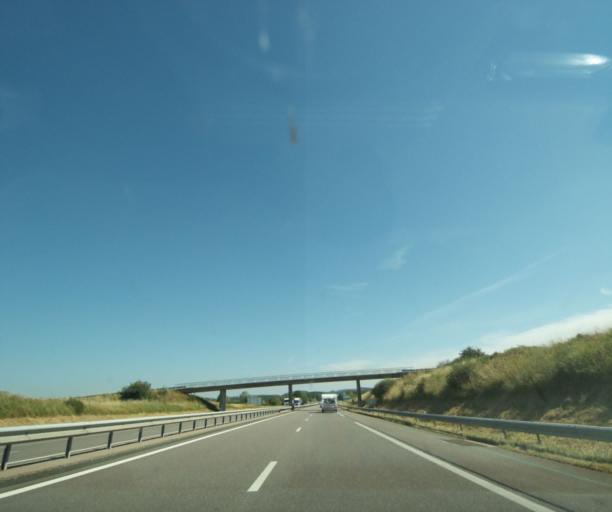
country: FR
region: Lorraine
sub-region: Departement des Vosges
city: Chatenois
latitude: 48.2867
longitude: 5.8556
